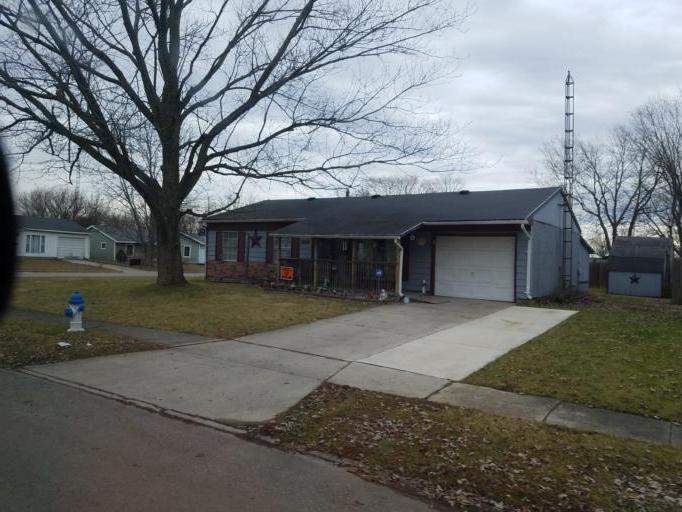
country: US
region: Ohio
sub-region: Marion County
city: Marion
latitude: 40.6121
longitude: -83.1202
